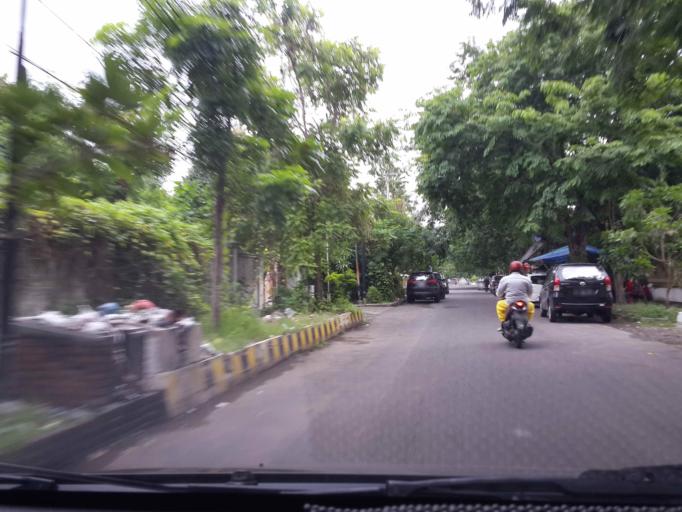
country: ID
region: East Java
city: Gubengairlangga
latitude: -7.2812
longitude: 112.7333
